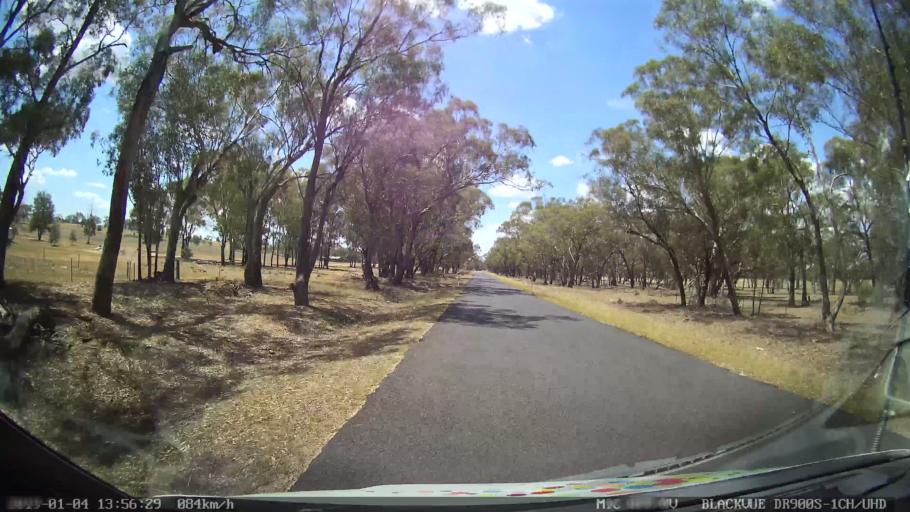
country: AU
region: New South Wales
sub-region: Dubbo Municipality
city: Dubbo
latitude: -32.3507
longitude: 148.5944
